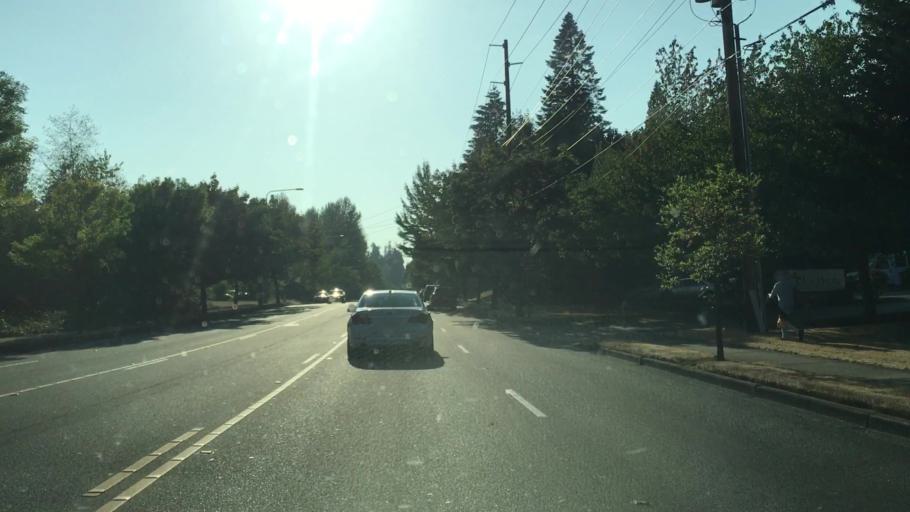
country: US
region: Washington
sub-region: King County
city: Federal Way
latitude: 47.2899
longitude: -122.3272
